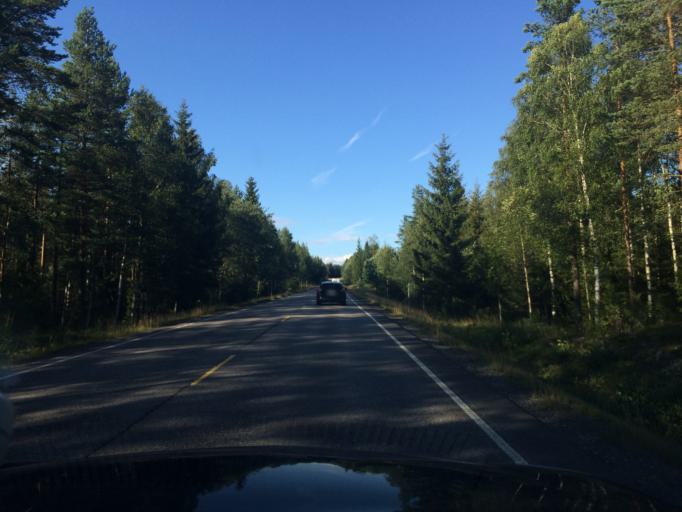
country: NO
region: Hedmark
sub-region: Elverum
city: Elverum
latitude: 61.0010
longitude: 11.7758
